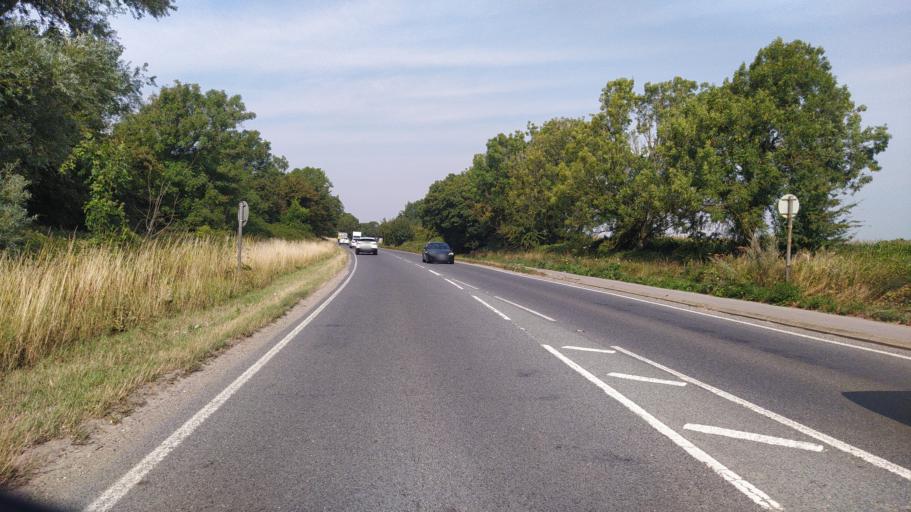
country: GB
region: England
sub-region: West Sussex
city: Bognor Regis
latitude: 50.8125
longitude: -0.7077
